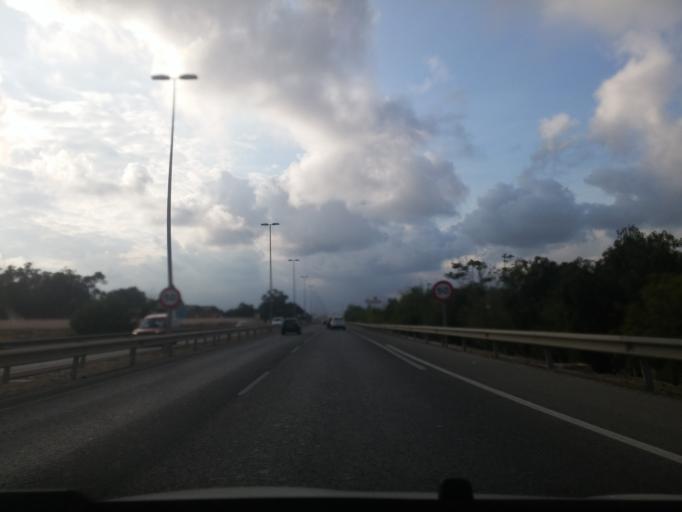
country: ES
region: Valencia
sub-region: Provincia de Alicante
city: San Vicent del Raspeig
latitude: 38.3704
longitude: -0.5042
